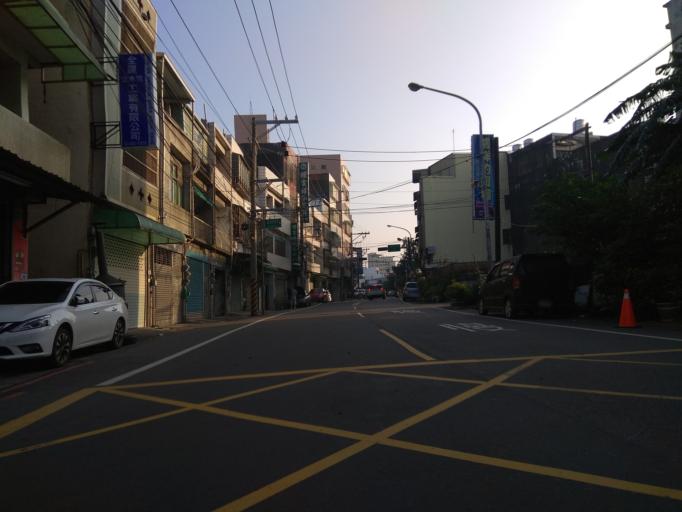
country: TW
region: Taiwan
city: Daxi
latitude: 24.9182
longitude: 121.1864
